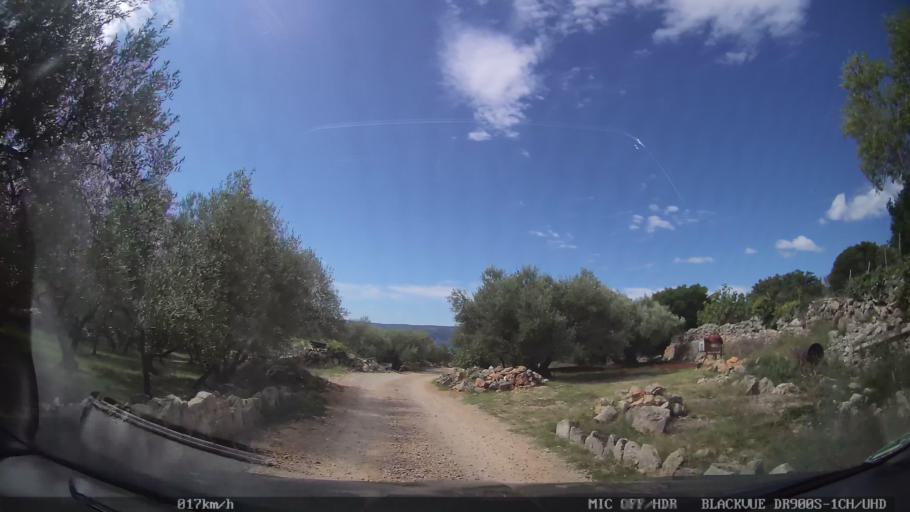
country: HR
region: Primorsko-Goranska
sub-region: Grad Krk
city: Krk
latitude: 45.0296
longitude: 14.5255
